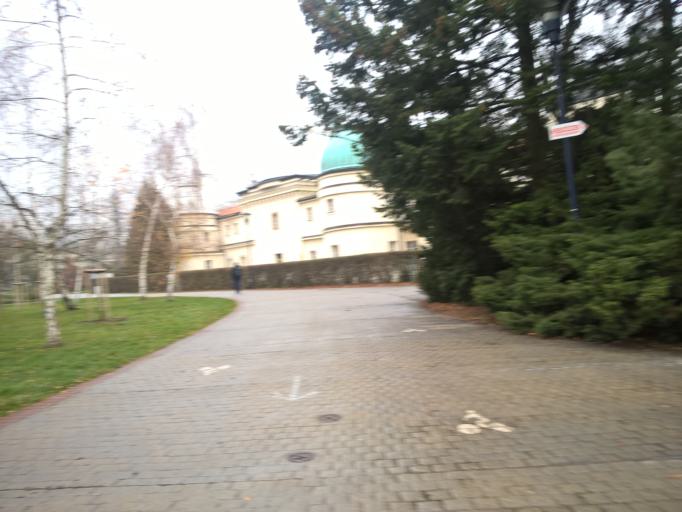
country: CZ
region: Praha
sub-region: Praha 1
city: Mala Strana
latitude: 50.0809
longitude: 14.3981
